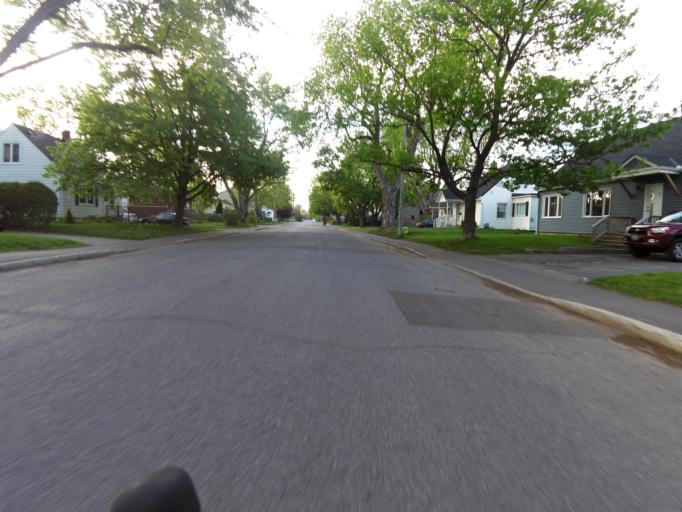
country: CA
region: Ontario
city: Ottawa
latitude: 45.3847
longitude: -75.7265
